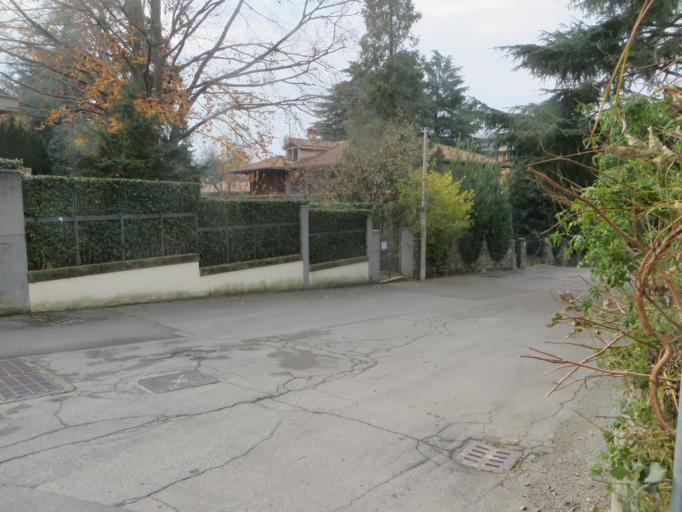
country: IT
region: Lombardy
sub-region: Provincia di Brescia
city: Brescia
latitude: 45.5449
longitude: 10.2322
